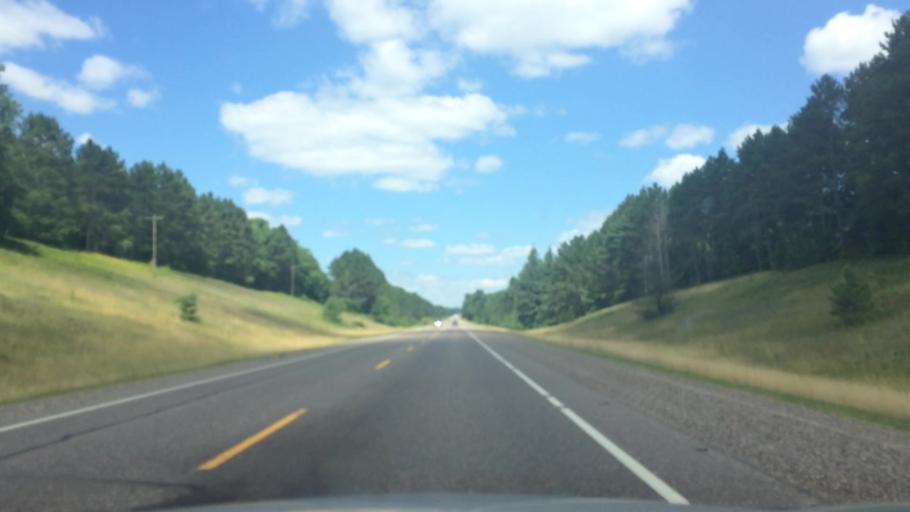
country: US
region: Wisconsin
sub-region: Vilas County
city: Lac du Flambeau
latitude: 45.9543
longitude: -89.7006
